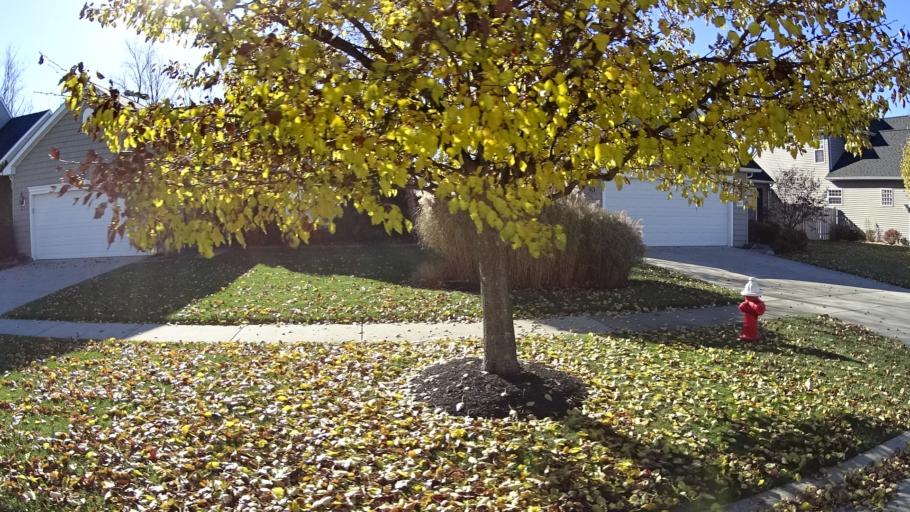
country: US
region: Ohio
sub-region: Lorain County
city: Avon
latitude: 41.4382
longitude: -82.0615
